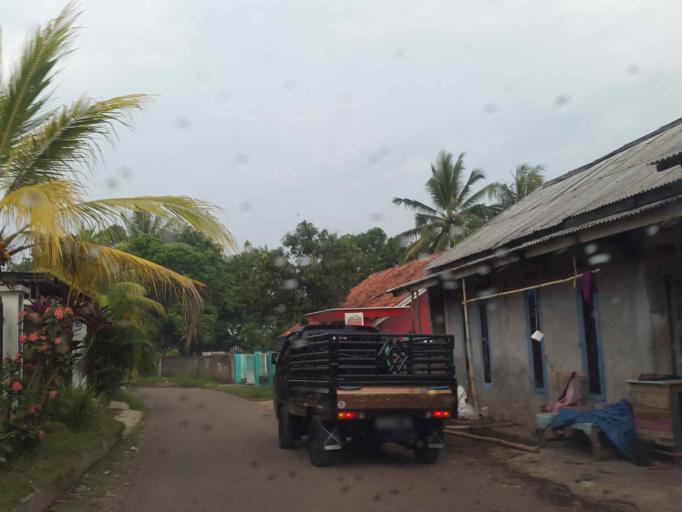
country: ID
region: West Java
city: Ciranjang-hilir
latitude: -6.7197
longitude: 107.2439
